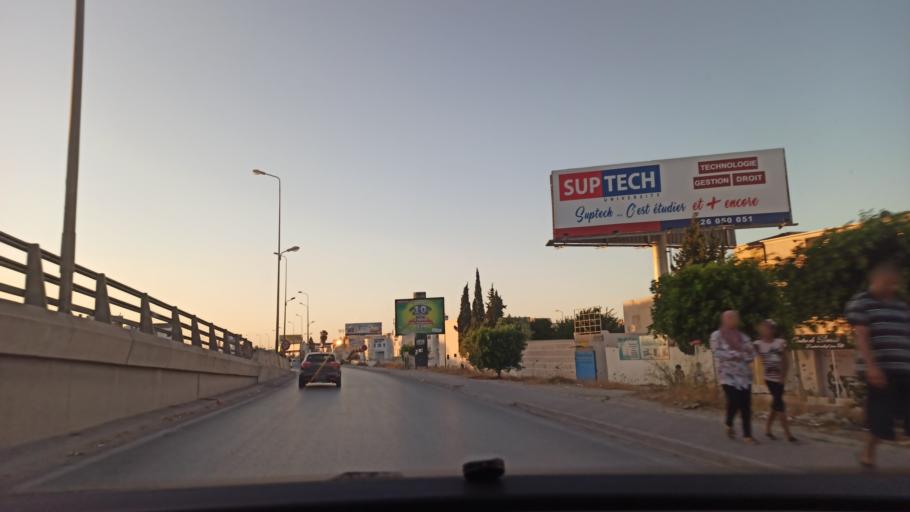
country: TN
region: Ariana
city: Ariana
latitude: 36.8606
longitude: 10.2027
